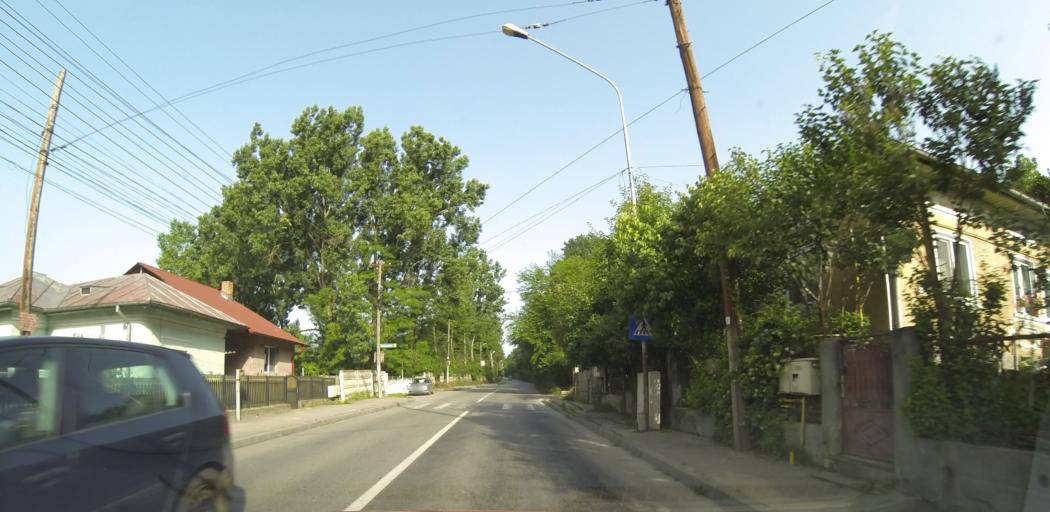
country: RO
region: Valcea
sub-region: Municipiul Ramnicu Valcea
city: Ramnicu Valcea
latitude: 45.1073
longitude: 24.3409
